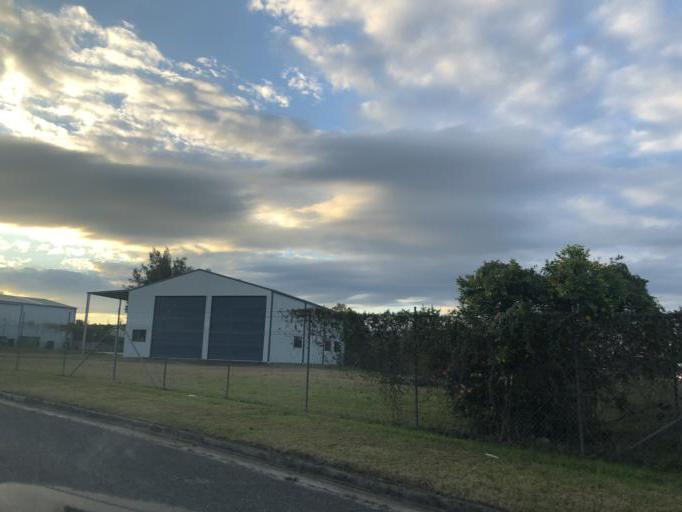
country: AU
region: New South Wales
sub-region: Nambucca Shire
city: Macksville
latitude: -30.7260
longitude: 152.9116
